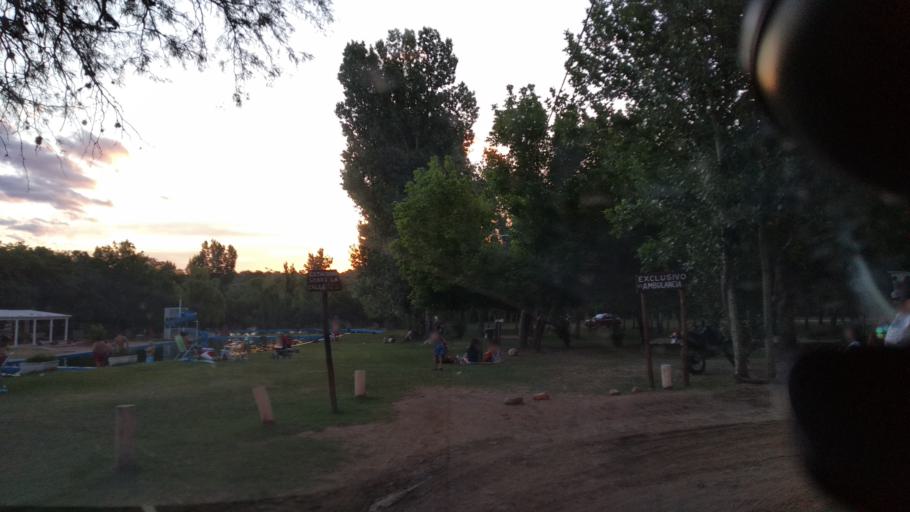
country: AR
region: Cordoba
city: Villa Las Rosas
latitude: -31.9445
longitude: -65.0692
